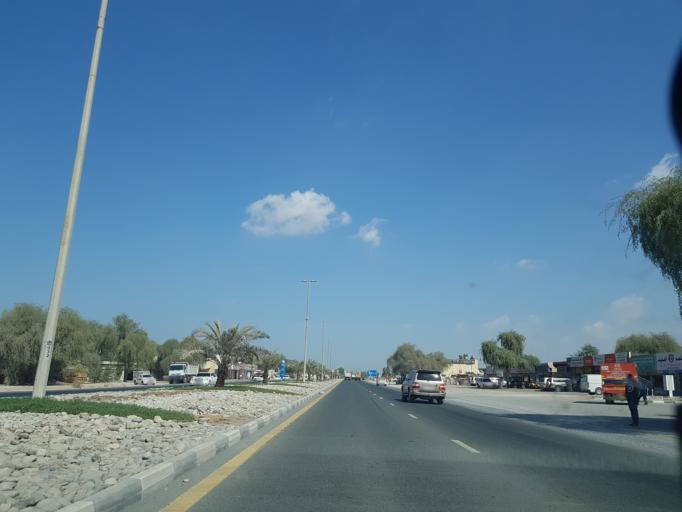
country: AE
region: Ra's al Khaymah
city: Ras al-Khaimah
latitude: 25.7079
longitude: 55.9699
